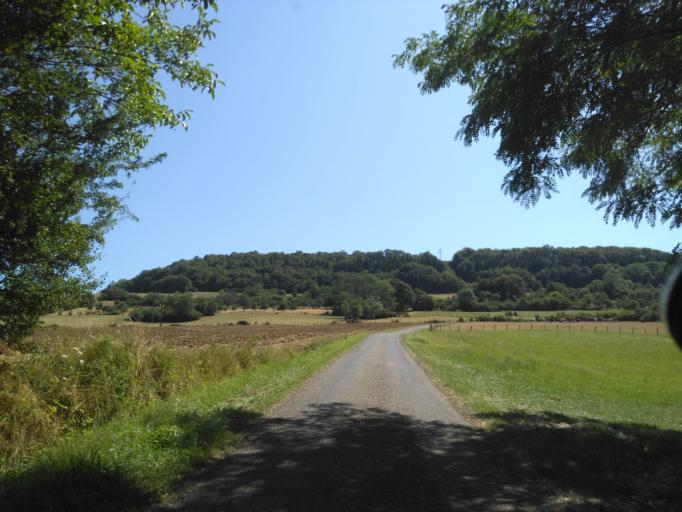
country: FR
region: Franche-Comte
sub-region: Departement de la Haute-Saone
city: Villersexel
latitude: 47.5070
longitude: 6.5233
